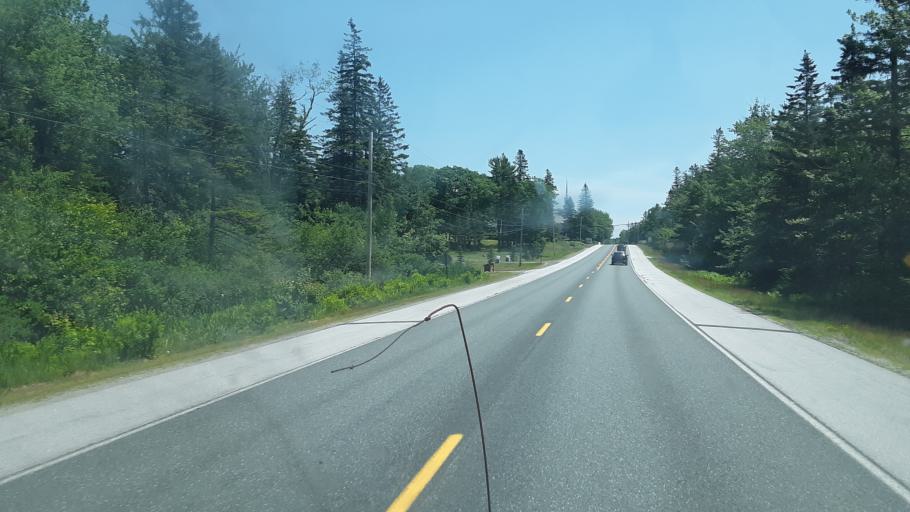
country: US
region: Maine
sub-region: Hancock County
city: Hancock
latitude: 44.5320
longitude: -68.2637
